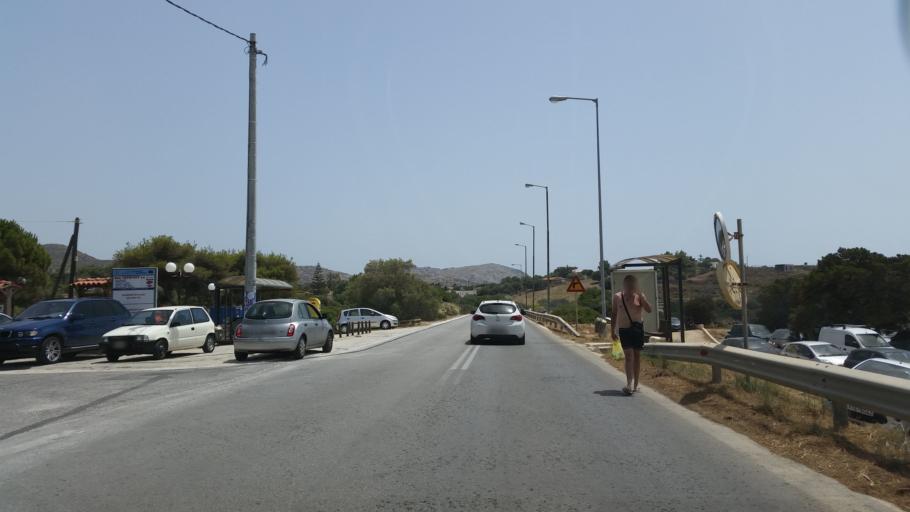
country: GR
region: Attica
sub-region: Nomarchia Anatolikis Attikis
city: Palaia Fokaia
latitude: 37.7026
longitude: 23.9401
